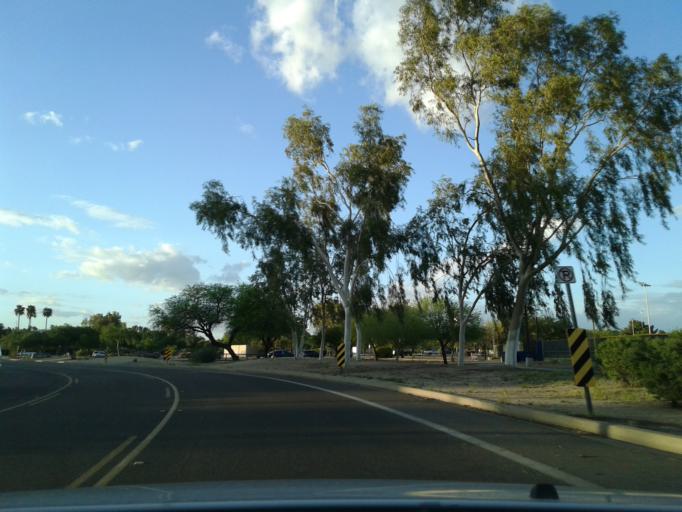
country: US
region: Arizona
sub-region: Maricopa County
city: Glendale
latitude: 33.5738
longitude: -112.1122
